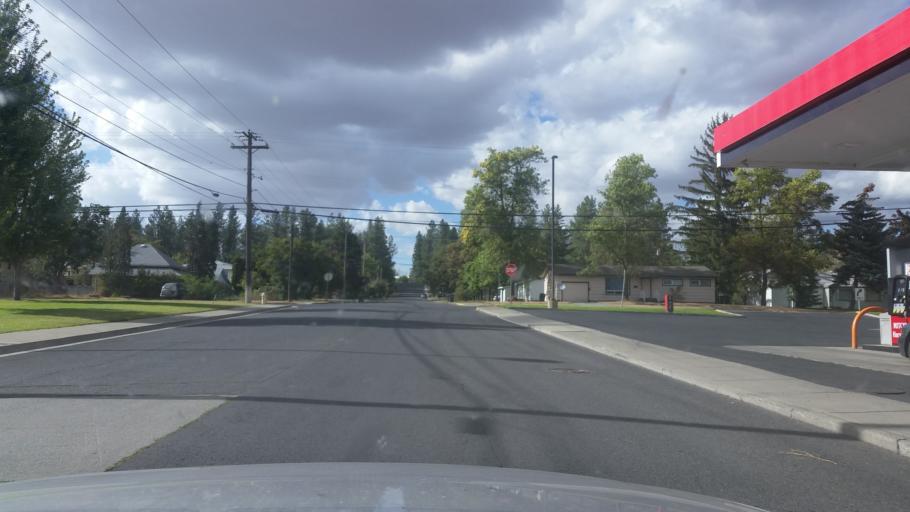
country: US
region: Washington
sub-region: Spokane County
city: Cheney
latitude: 47.4828
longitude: -117.5822
